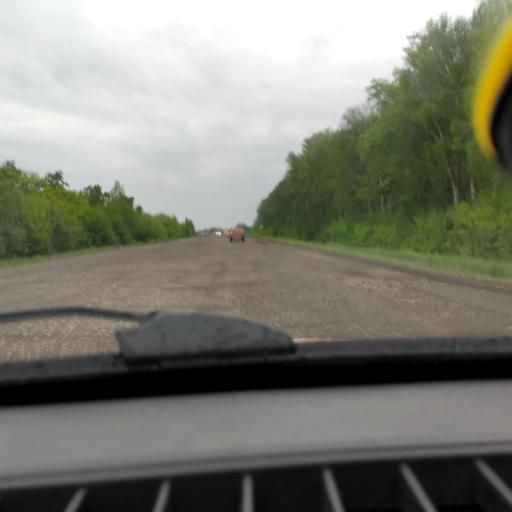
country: RU
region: Samara
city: Tol'yatti
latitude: 53.6540
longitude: 49.4240
